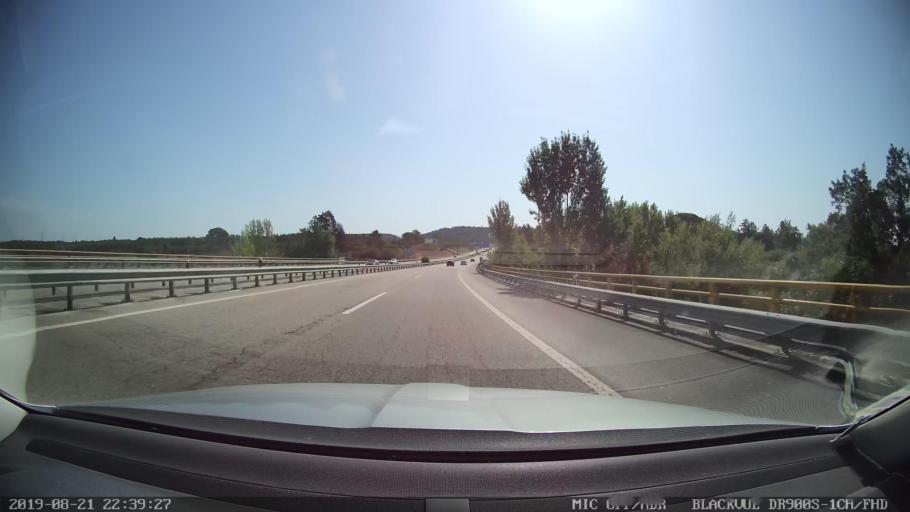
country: PT
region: Santarem
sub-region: Entroncamento
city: Entroncamento
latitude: 39.4892
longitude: -8.4570
